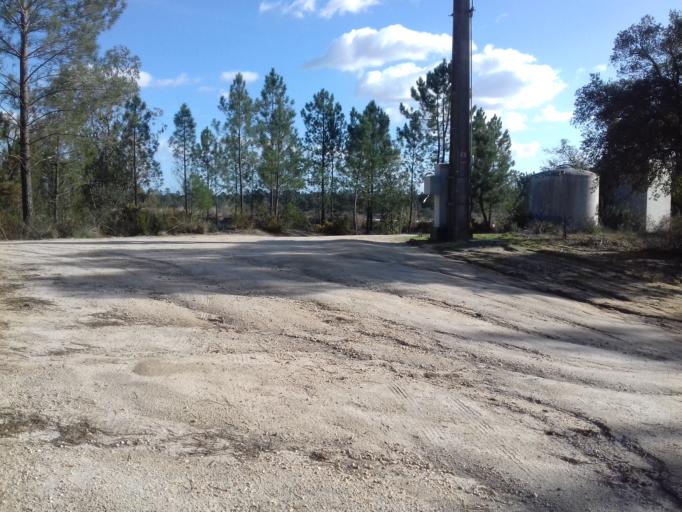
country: PT
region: Santarem
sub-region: Coruche
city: Coruche
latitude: 39.0158
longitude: -8.5480
